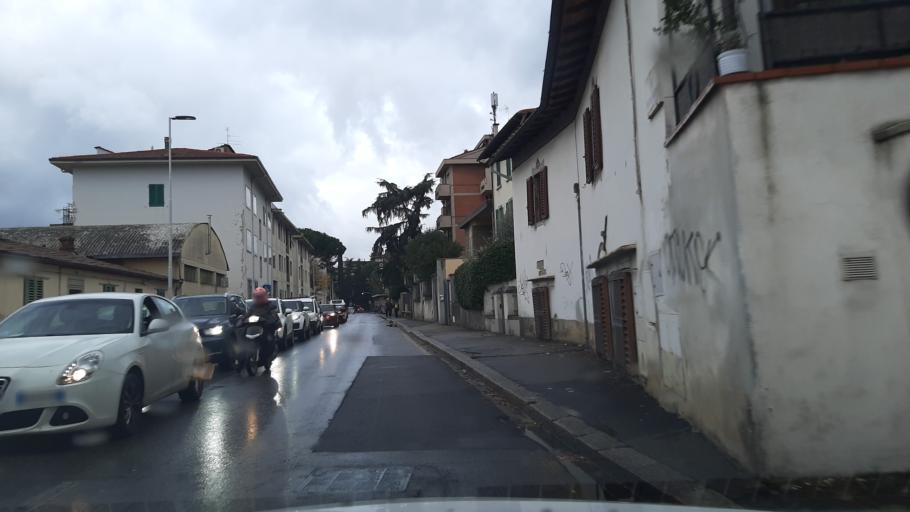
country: IT
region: Tuscany
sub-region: Province of Florence
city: Florence
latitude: 43.8042
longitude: 11.2441
